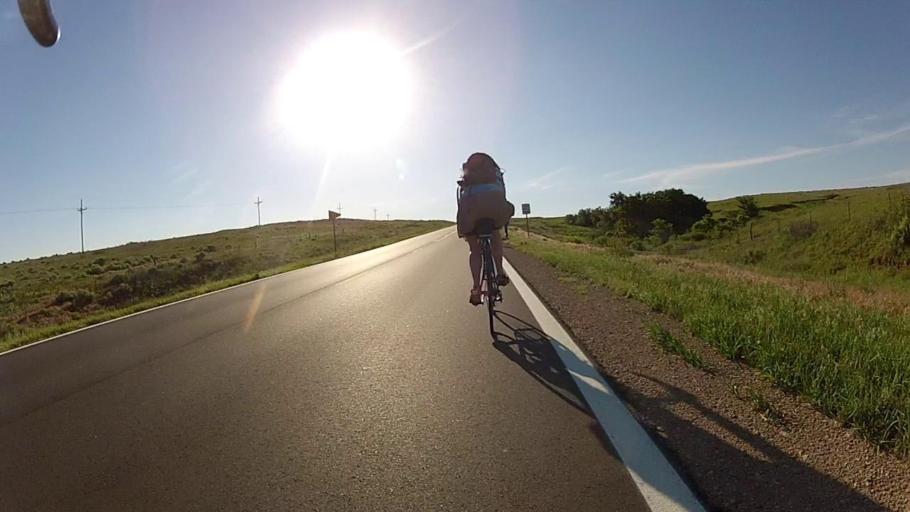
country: US
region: Kansas
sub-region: Comanche County
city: Coldwater
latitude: 37.2806
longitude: -99.0256
